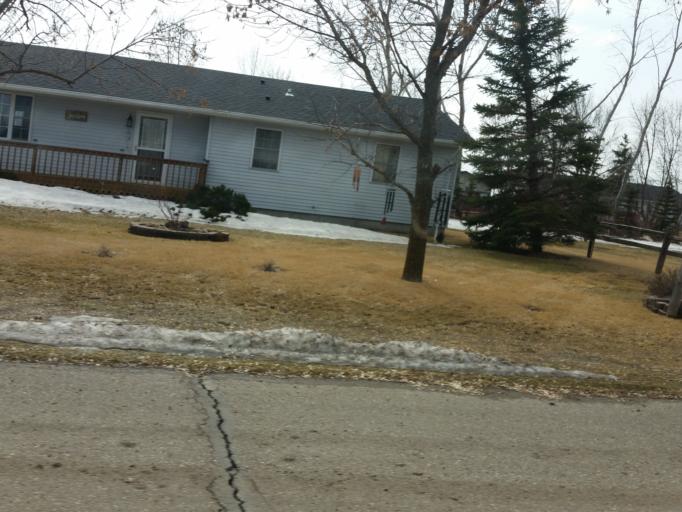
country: US
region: North Dakota
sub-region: Walsh County
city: Grafton
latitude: 48.2925
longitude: -97.3811
